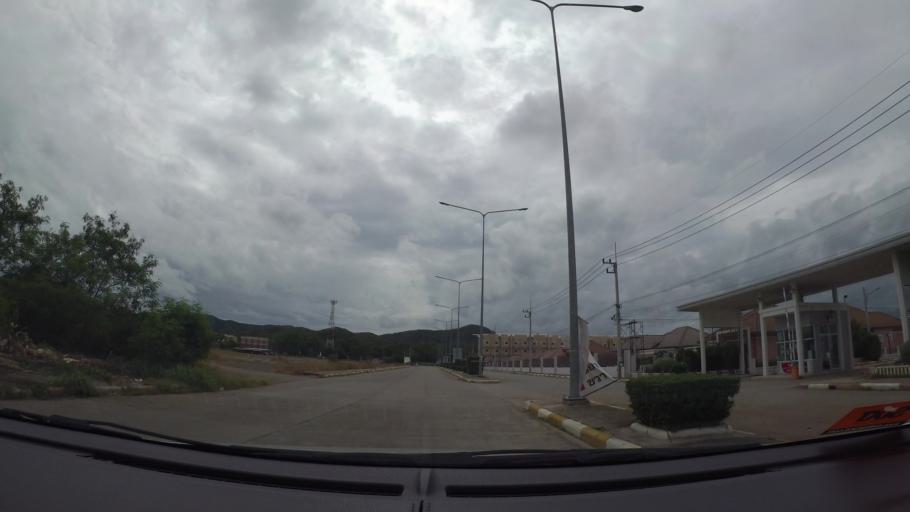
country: TH
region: Chon Buri
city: Sattahip
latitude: 12.7256
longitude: 100.8916
